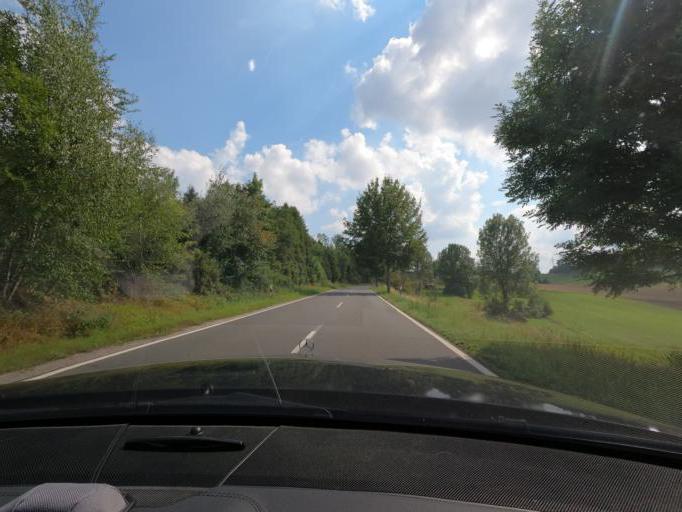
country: DE
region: Lower Saxony
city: Bad Lauterberg im Harz
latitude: 51.6187
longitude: 10.4655
